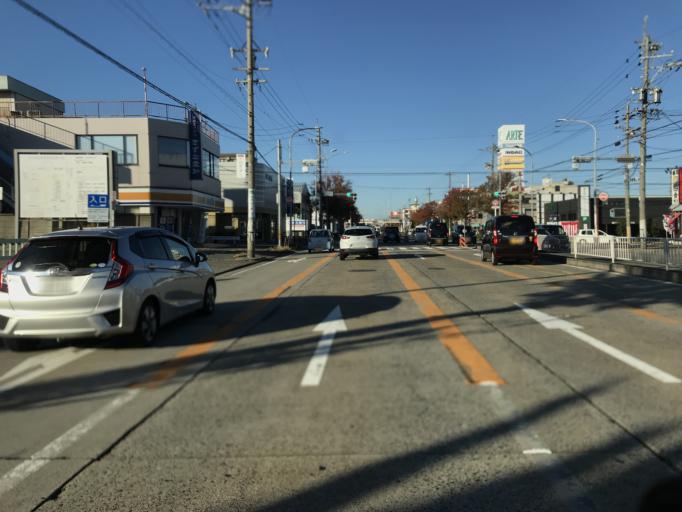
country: JP
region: Aichi
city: Nagoya-shi
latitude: 35.1277
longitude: 136.8690
